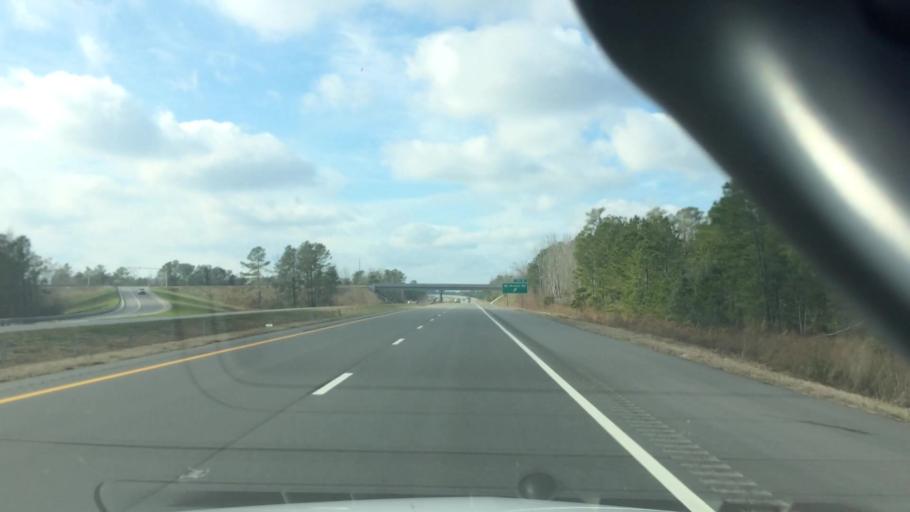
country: US
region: North Carolina
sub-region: Brunswick County
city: Leland
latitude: 34.2769
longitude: -78.0452
